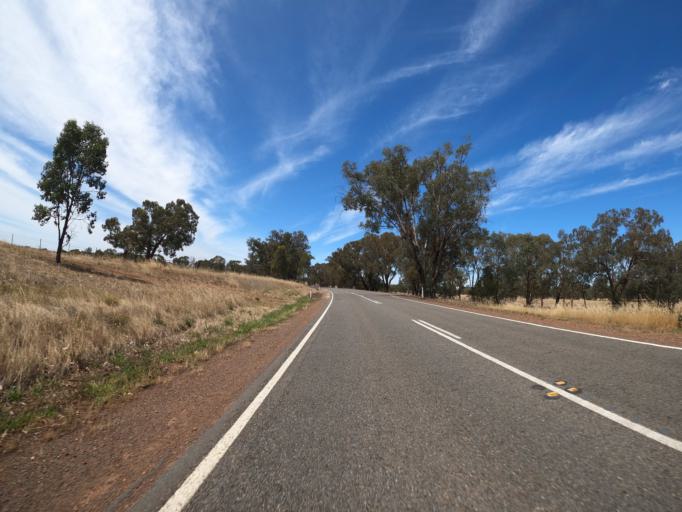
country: AU
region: Victoria
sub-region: Benalla
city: Benalla
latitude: -36.3421
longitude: 145.9591
